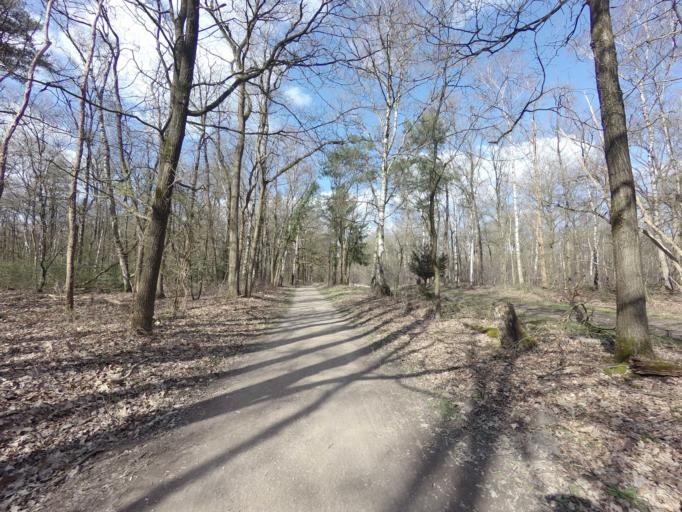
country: NL
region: North Holland
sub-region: Gemeente Bussum
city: Bussum
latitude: 52.2536
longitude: 5.1437
